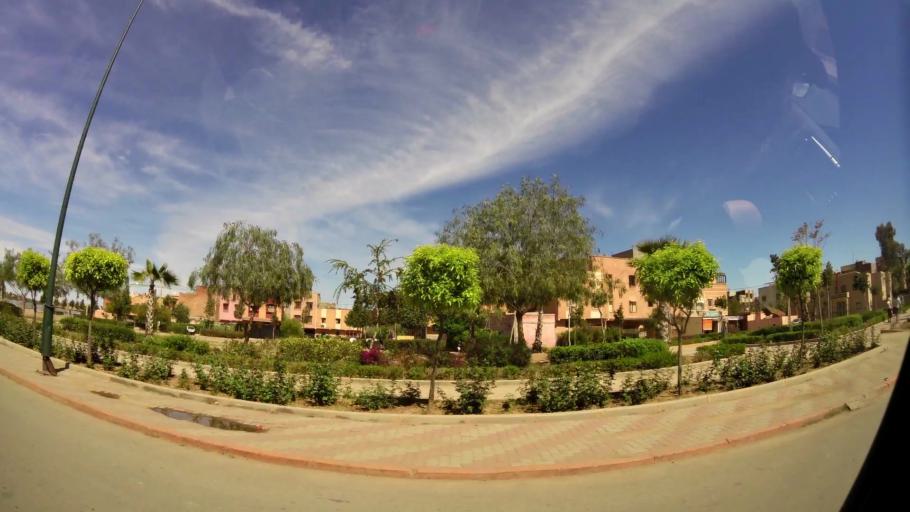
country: MA
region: Marrakech-Tensift-Al Haouz
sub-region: Marrakech
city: Marrakesh
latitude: 31.6007
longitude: -7.9618
